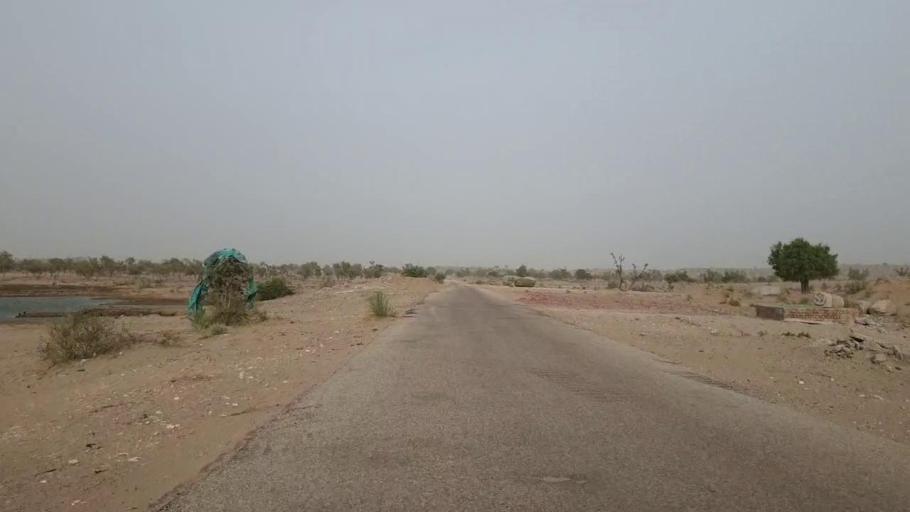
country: PK
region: Sindh
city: Islamkot
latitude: 24.5458
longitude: 70.3710
